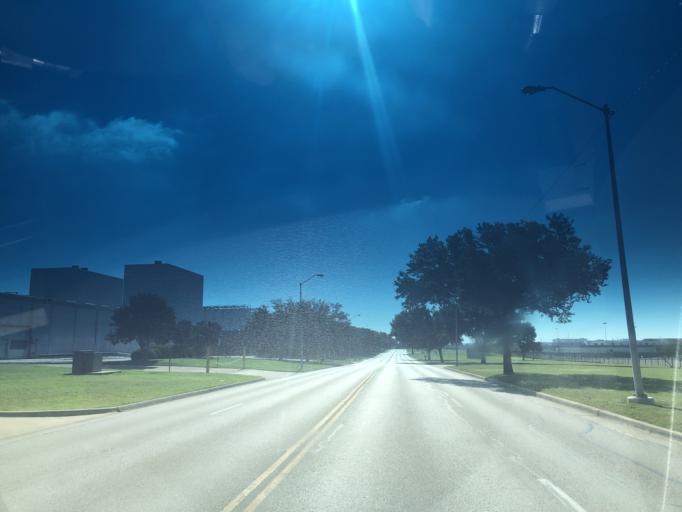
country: US
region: Texas
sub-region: Dallas County
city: Grand Prairie
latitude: 32.7205
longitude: -97.0360
